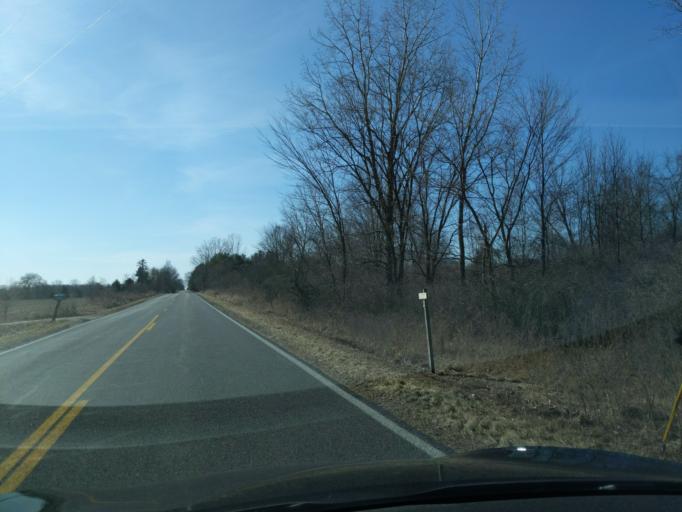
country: US
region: Michigan
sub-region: Ionia County
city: Saranac
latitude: 42.9297
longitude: -85.1406
